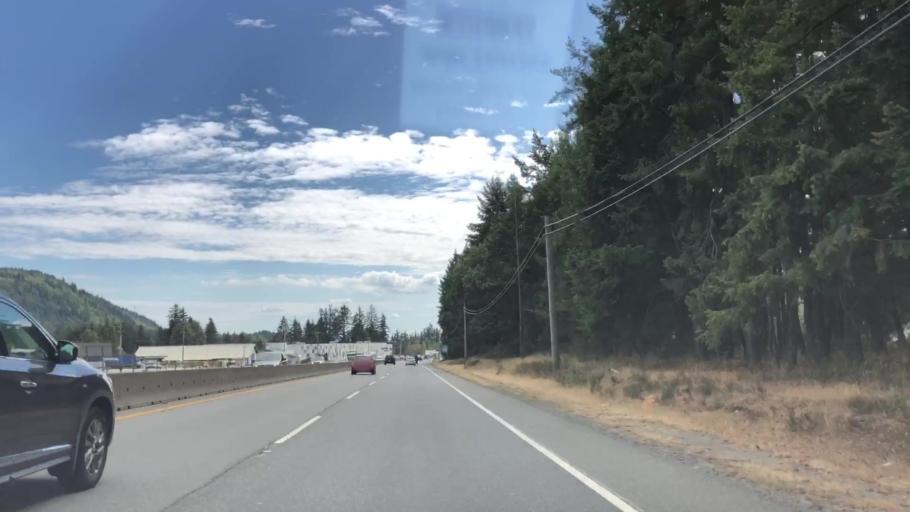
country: CA
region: British Columbia
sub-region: Cowichan Valley Regional District
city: Ladysmith
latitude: 49.0402
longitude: -123.8674
